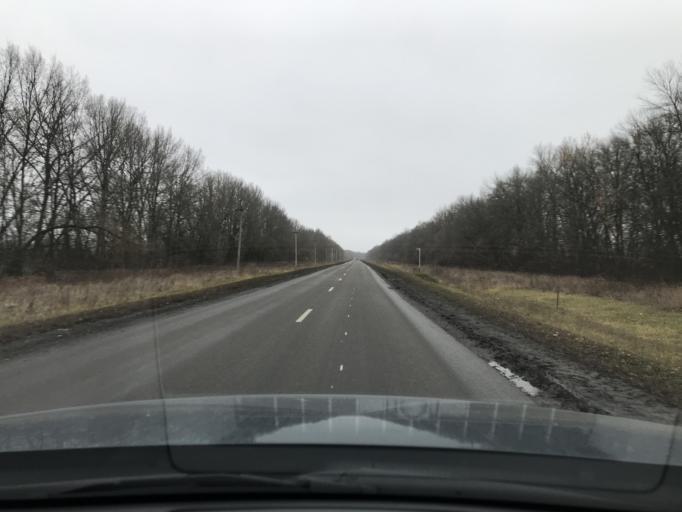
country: RU
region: Penza
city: Zemetchino
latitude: 53.5343
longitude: 42.6608
